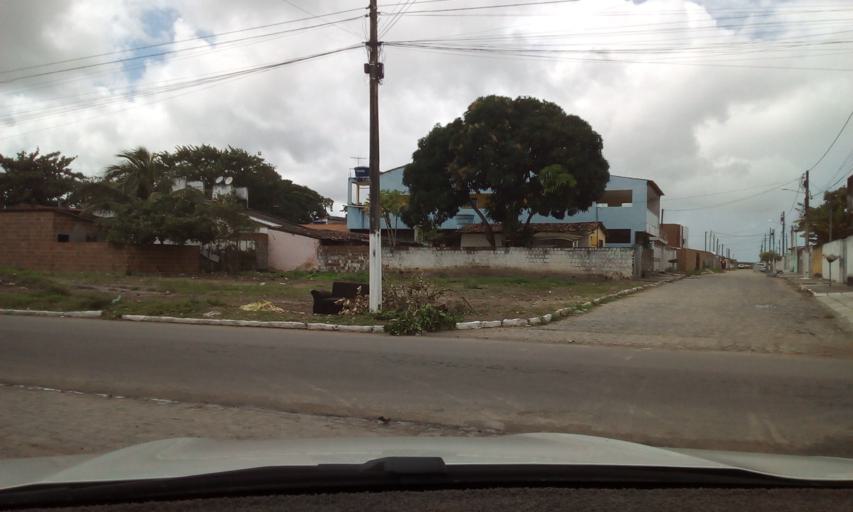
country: BR
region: Paraiba
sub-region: Santa Rita
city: Santa Rita
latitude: -7.1408
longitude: -34.9653
